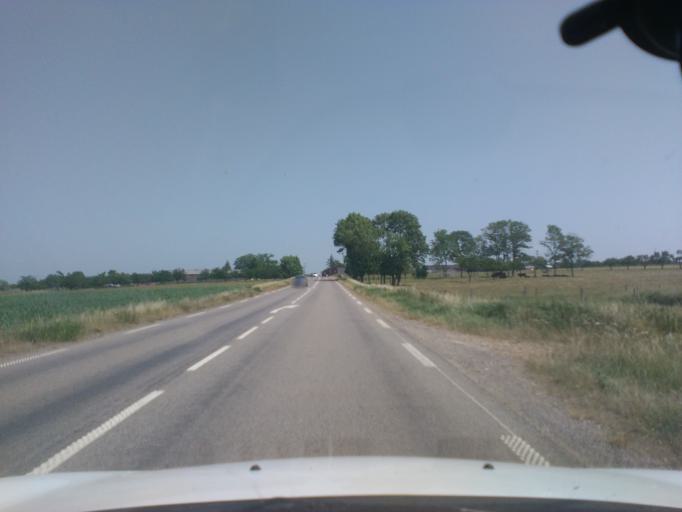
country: FR
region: Lorraine
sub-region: Departement des Vosges
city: Vittel
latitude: 48.3090
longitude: 5.9654
